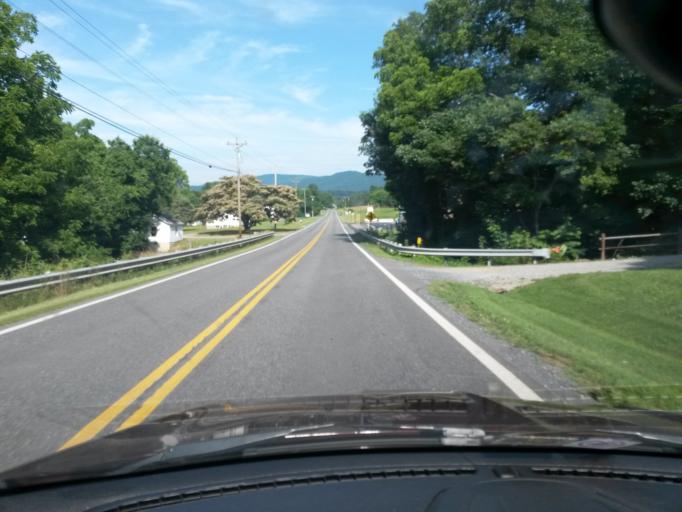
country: US
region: Virginia
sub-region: Rockingham County
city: Broadway
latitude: 38.6623
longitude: -78.9151
